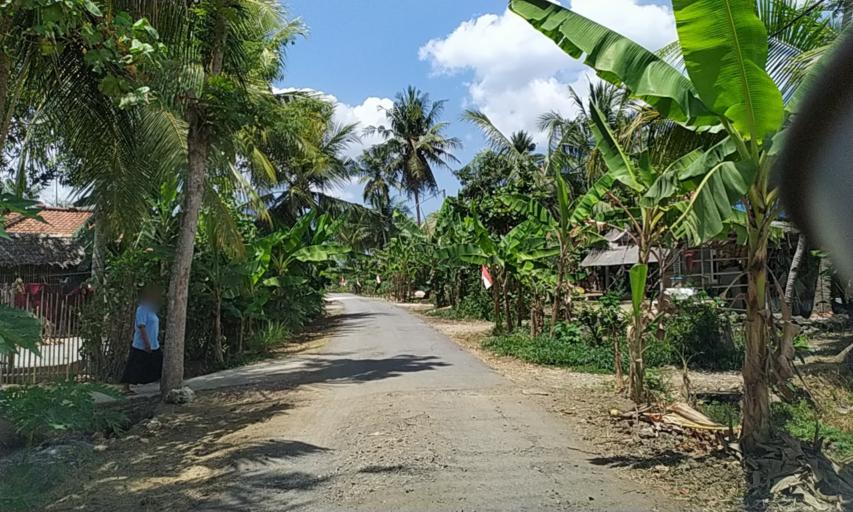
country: ID
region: Central Java
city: Kedungsalam
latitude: -7.6123
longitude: 108.7669
